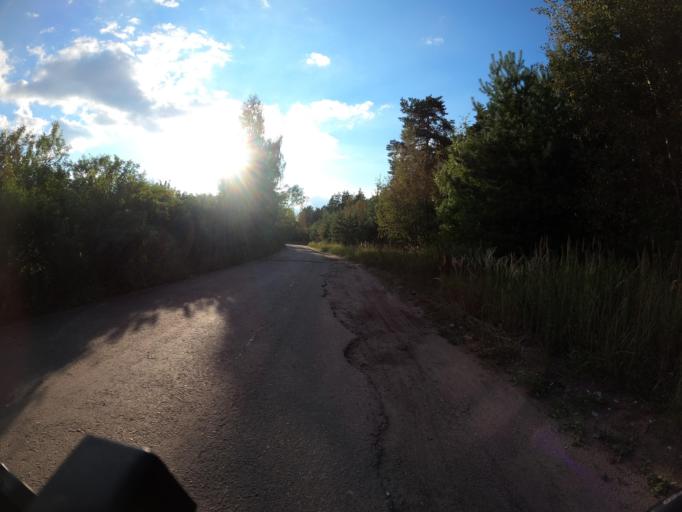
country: RU
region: Moskovskaya
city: Beloozerskiy
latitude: 55.4532
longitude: 38.4984
